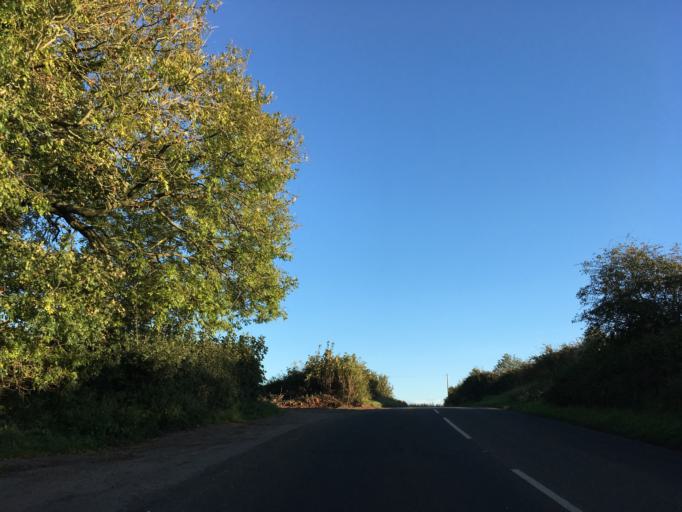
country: GB
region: England
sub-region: South Gloucestershire
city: Alveston
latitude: 51.5935
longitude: -2.5610
